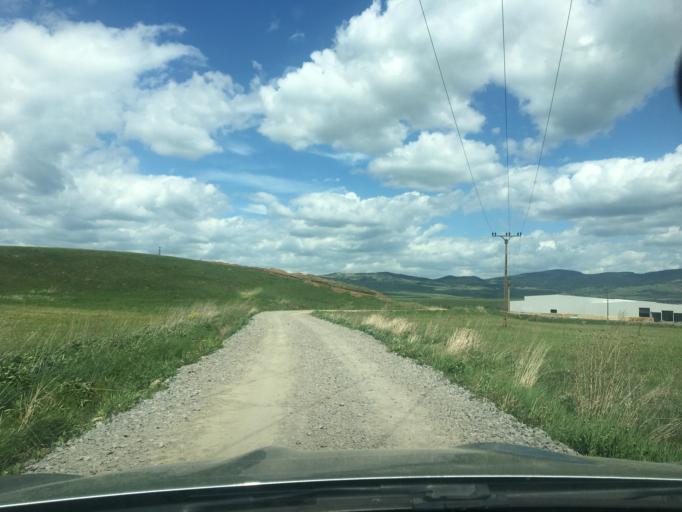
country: RO
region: Harghita
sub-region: Comuna Remetea
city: Remetea
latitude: 46.8138
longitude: 25.4537
